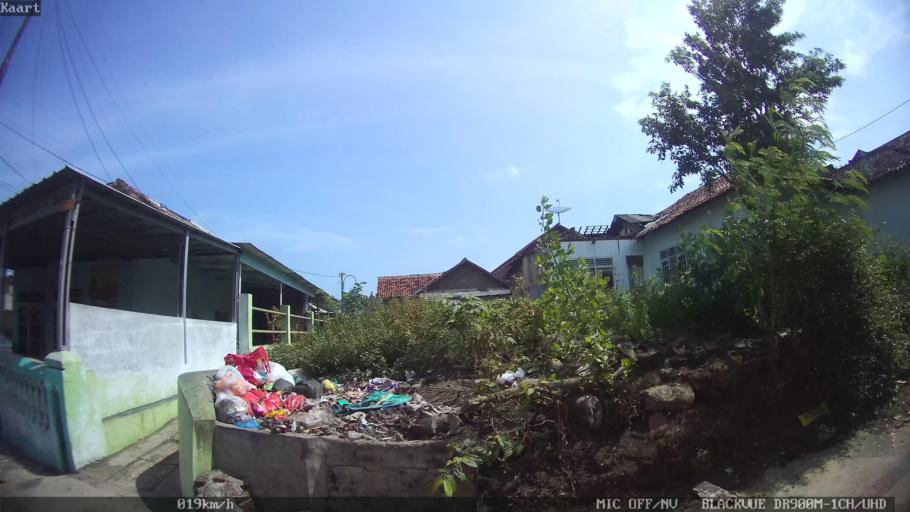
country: ID
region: Lampung
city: Kedaton
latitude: -5.3973
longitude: 105.2549
